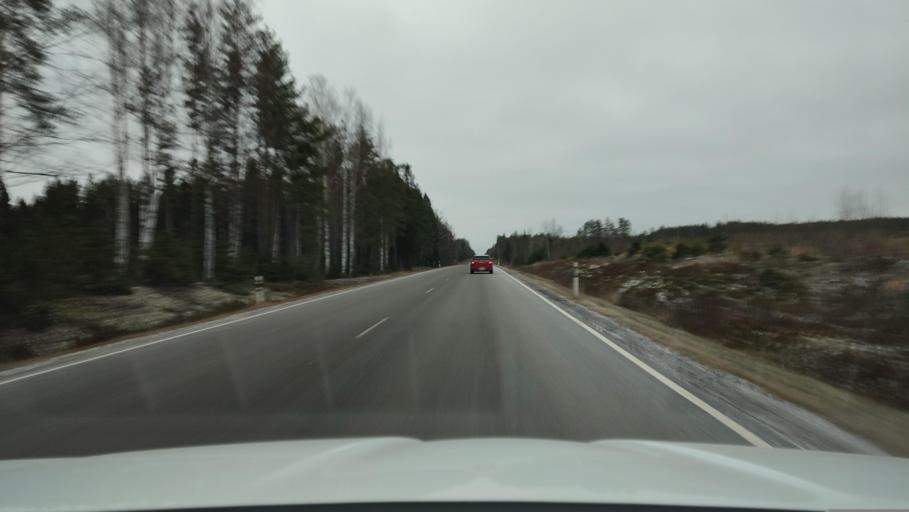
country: FI
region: Ostrobothnia
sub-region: Sydosterbotten
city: Naerpes
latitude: 62.5721
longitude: 21.4877
